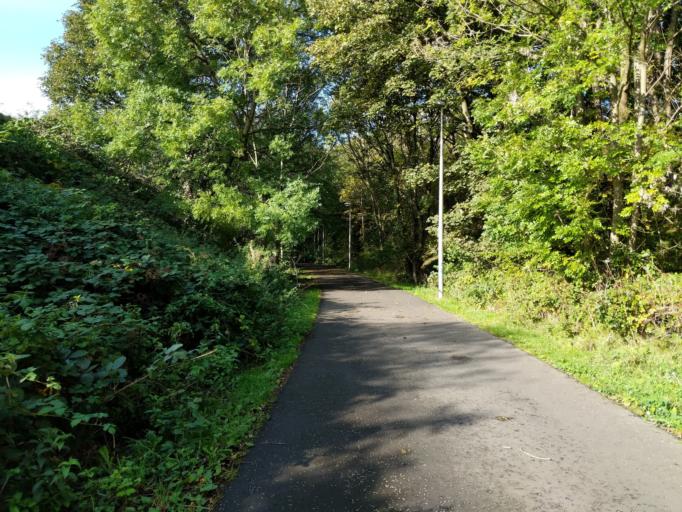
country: GB
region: Scotland
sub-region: Edinburgh
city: Edinburgh
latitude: 55.9718
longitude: -3.1950
